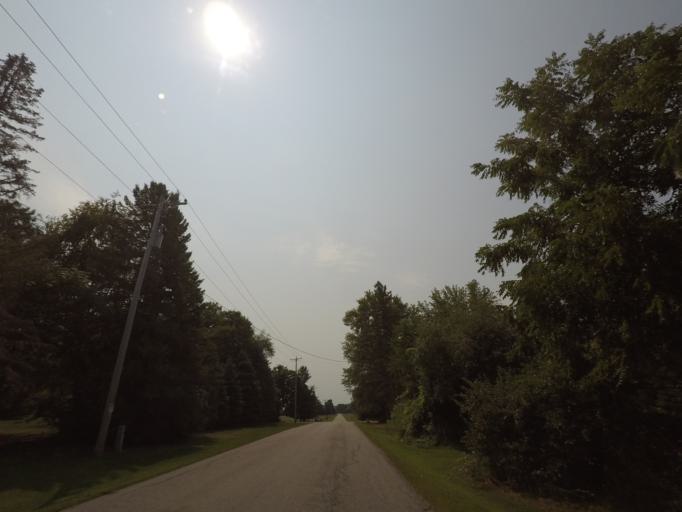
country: US
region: Wisconsin
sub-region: Waukesha County
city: Oconomowoc
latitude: 43.0670
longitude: -88.5552
